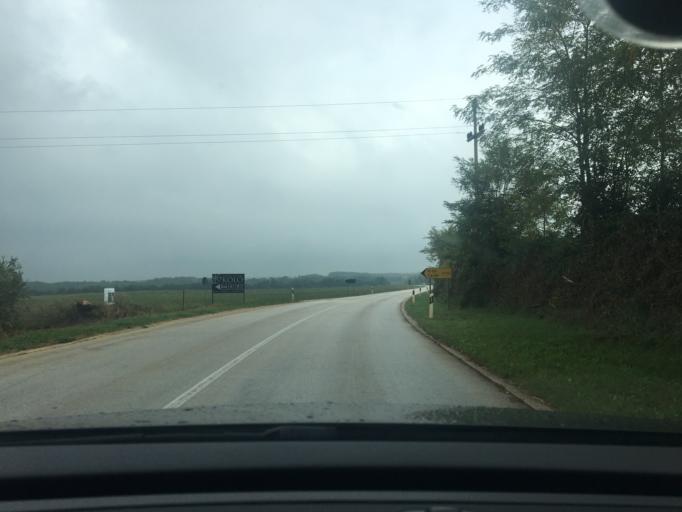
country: HR
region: Istarska
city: Novigrad
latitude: 45.3489
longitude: 13.5960
